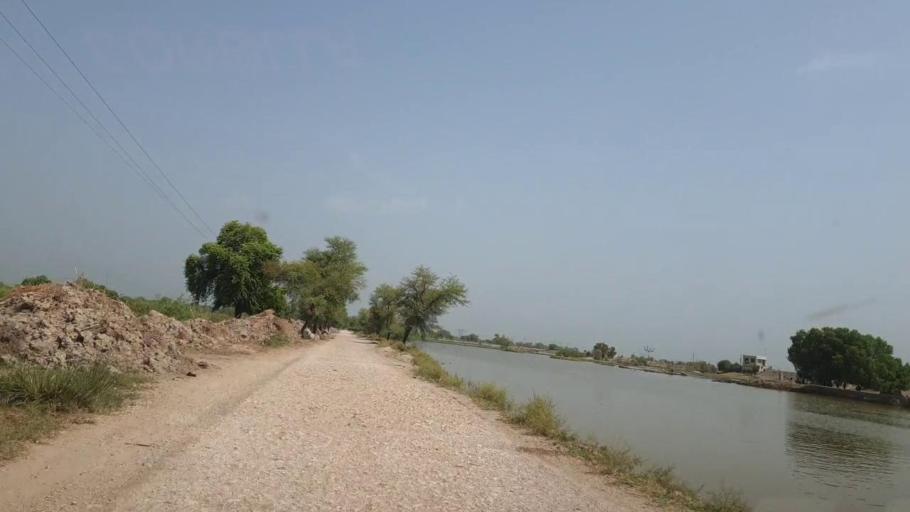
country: PK
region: Sindh
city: Lakhi
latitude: 27.8734
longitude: 68.6592
